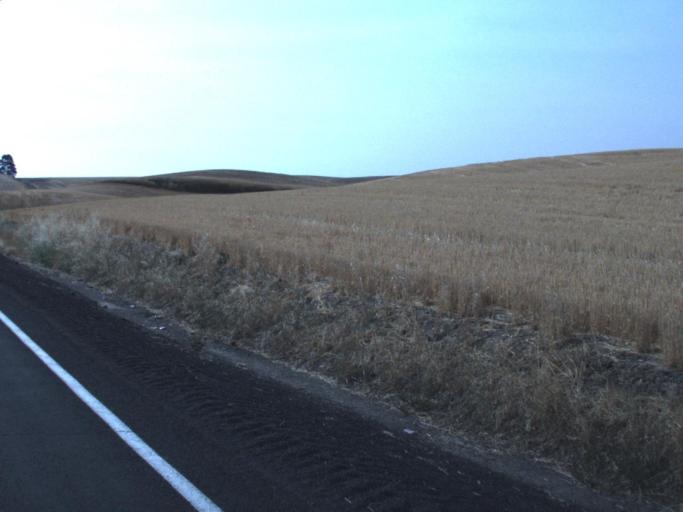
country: US
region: Idaho
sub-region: Latah County
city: Moscow
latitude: 46.9562
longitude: -117.0894
